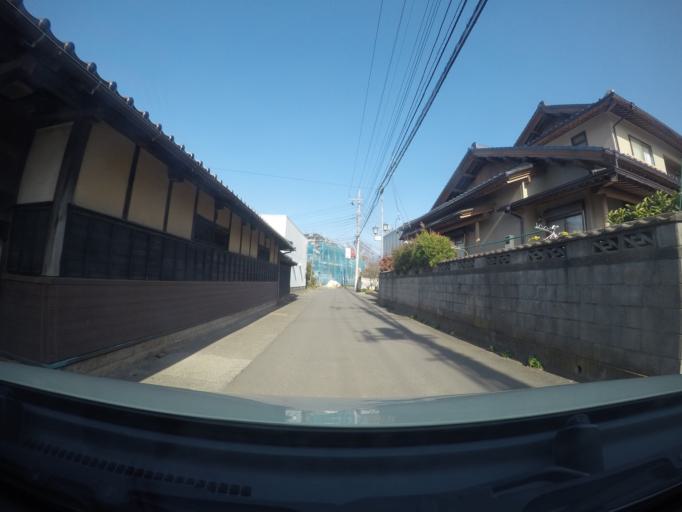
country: JP
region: Ibaraki
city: Tsukuba
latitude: 36.1256
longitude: 140.1209
